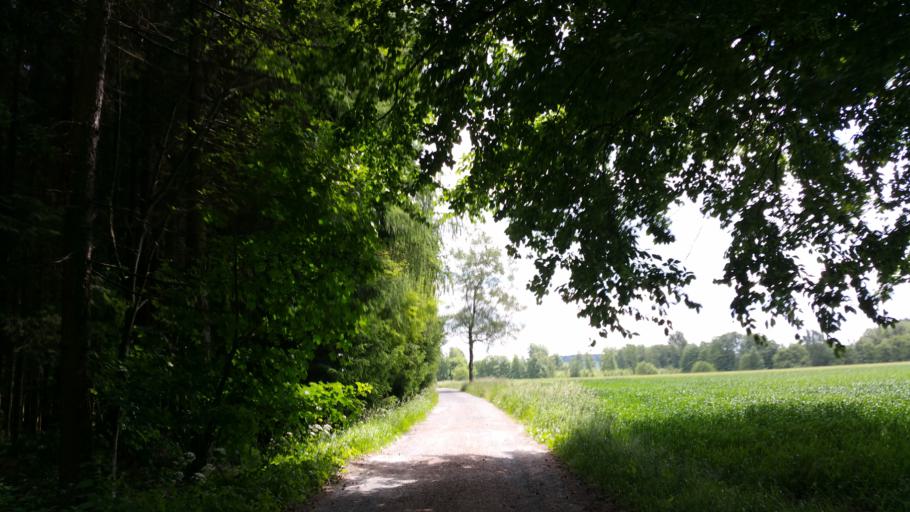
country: DE
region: Bavaria
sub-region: Upper Franconia
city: Kirchenlamitz
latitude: 50.1645
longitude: 11.9382
